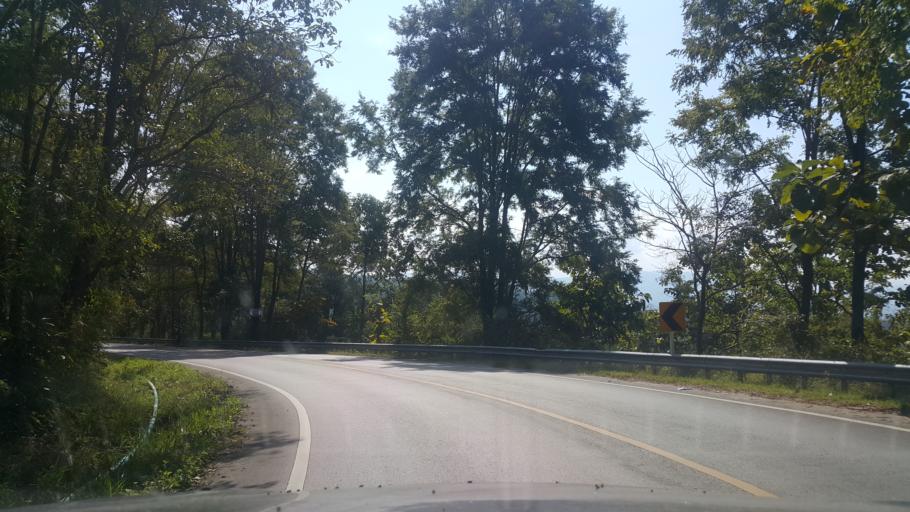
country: TH
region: Chiang Mai
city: Samoeng
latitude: 18.8540
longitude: 98.7716
